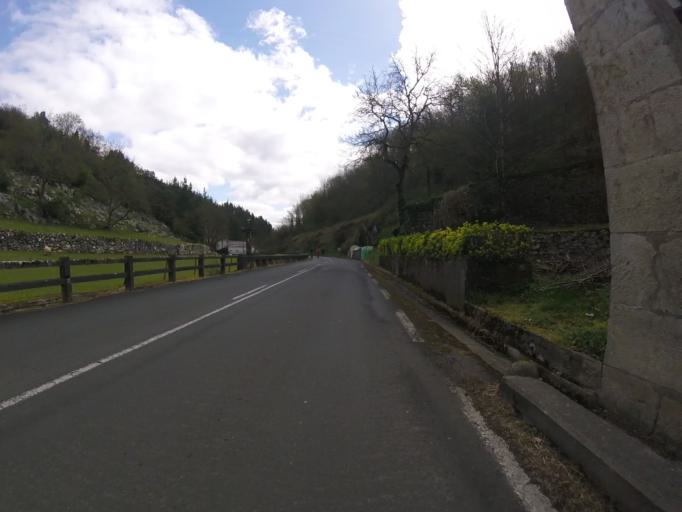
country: ES
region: Basque Country
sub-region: Provincia de Guipuzcoa
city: Albiztur
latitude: 43.1286
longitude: -2.1279
